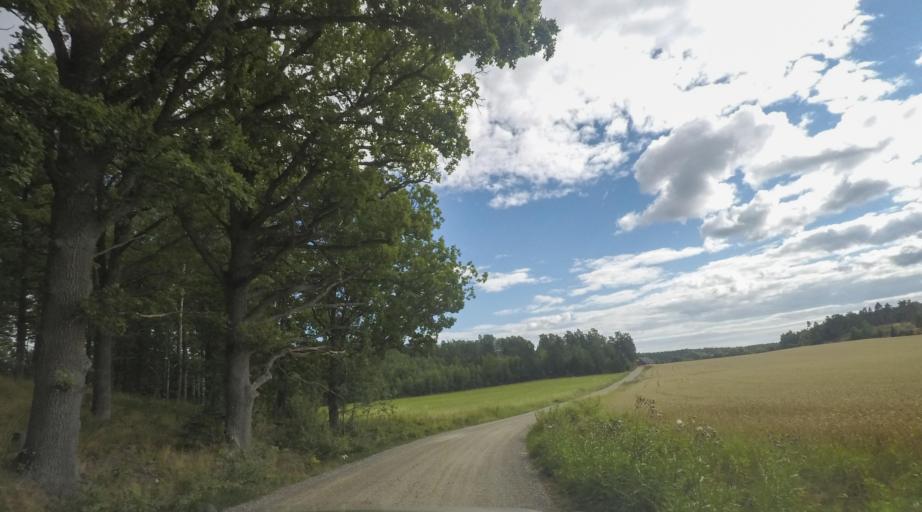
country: SE
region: Stockholm
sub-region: Sodertalje Kommun
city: Pershagen
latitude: 59.1196
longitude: 17.6566
